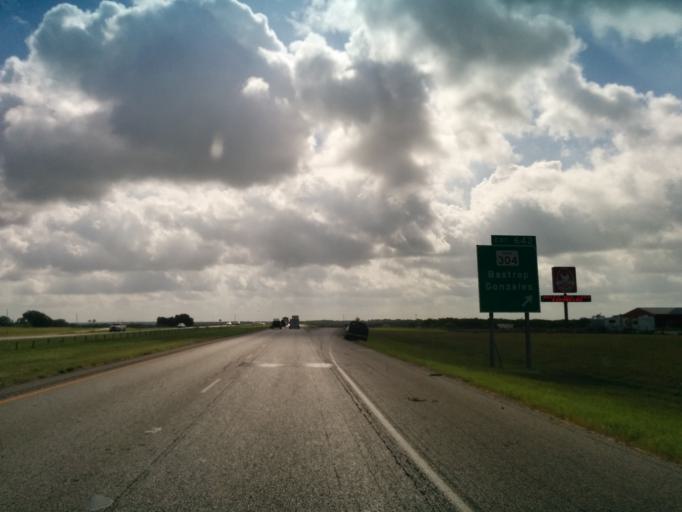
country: US
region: Texas
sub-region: Gonzales County
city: Waelder
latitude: 29.6575
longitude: -97.4215
